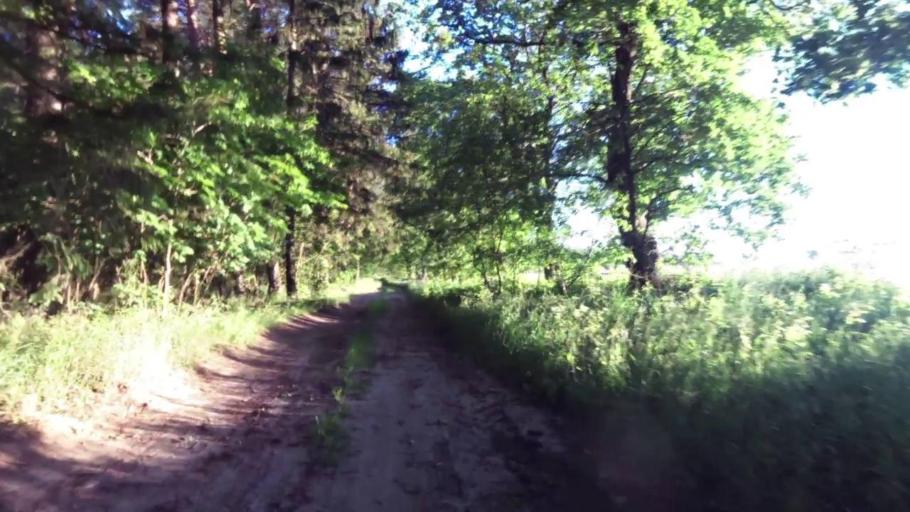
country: PL
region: West Pomeranian Voivodeship
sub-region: Powiat bialogardzki
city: Bialogard
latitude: 54.0578
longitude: 16.1020
